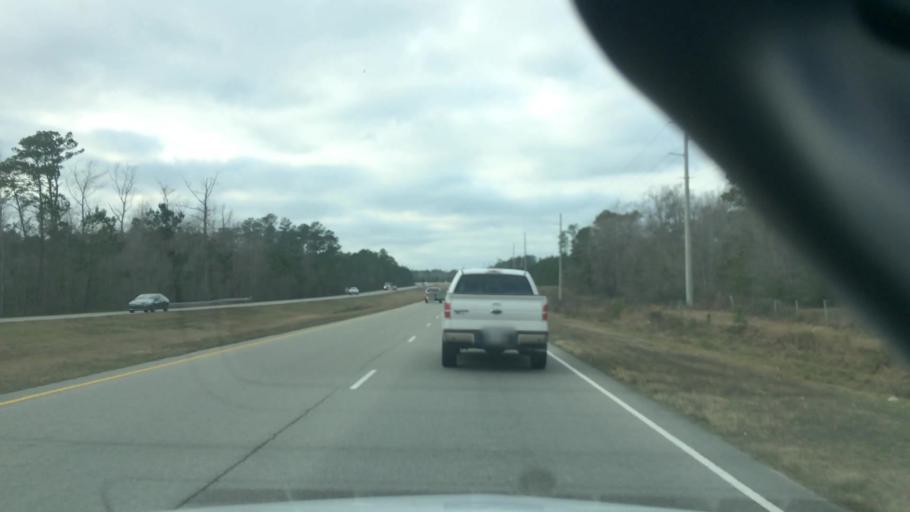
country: US
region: North Carolina
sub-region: Brunswick County
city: Shallotte
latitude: 33.9884
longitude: -78.3756
